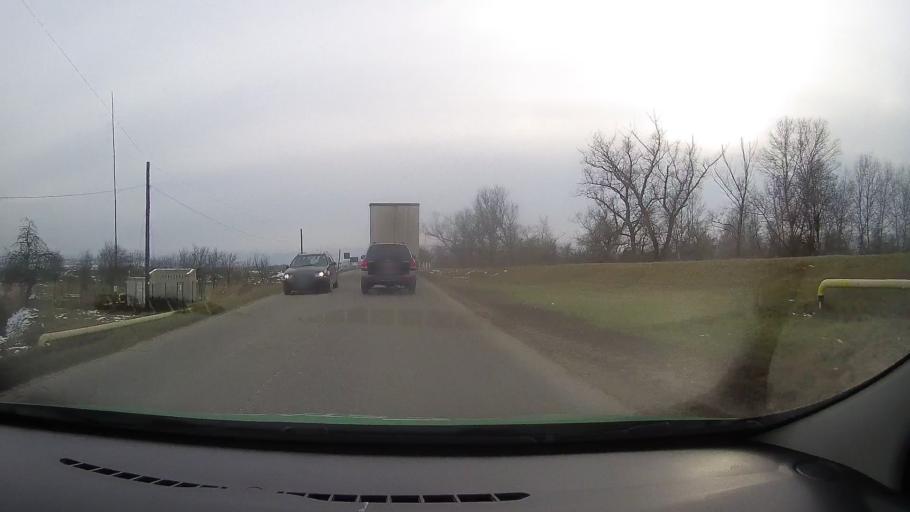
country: RO
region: Hunedoara
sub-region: Comuna Geoagiu
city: Geoagiu
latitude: 45.8995
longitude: 23.2249
